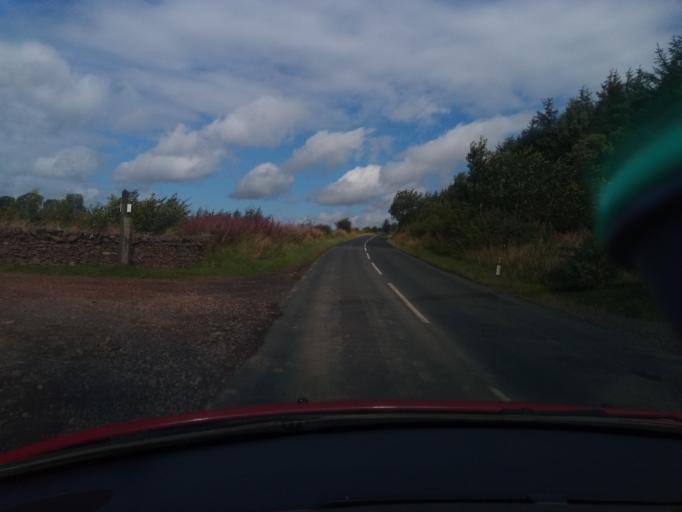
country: GB
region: Scotland
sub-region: The Scottish Borders
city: Melrose
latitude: 55.5716
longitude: -2.7317
